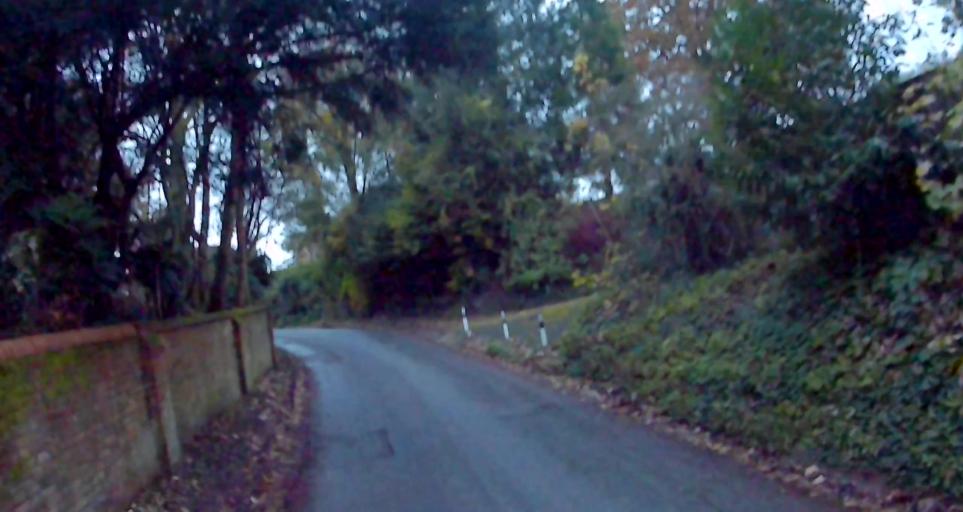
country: GB
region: England
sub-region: Hampshire
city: Old Basing
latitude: 51.2321
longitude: -1.0041
